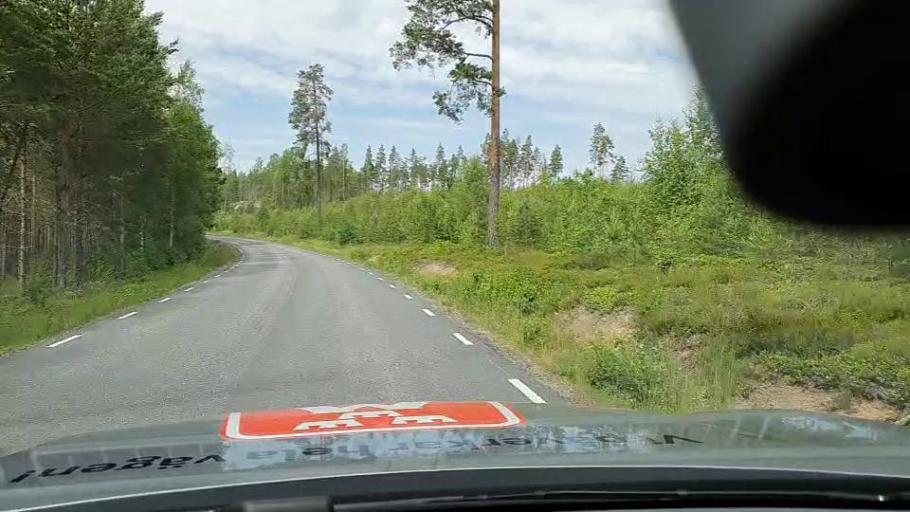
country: SE
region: Soedermanland
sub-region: Eskilstuna Kommun
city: Arla
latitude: 59.2454
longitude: 16.7179
